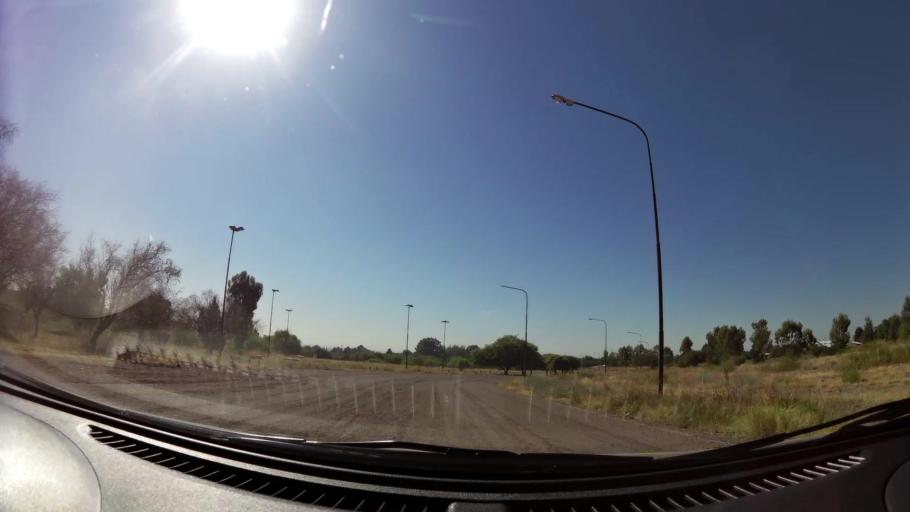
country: AR
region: Mendoza
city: Mendoza
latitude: -32.8981
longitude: -68.8821
